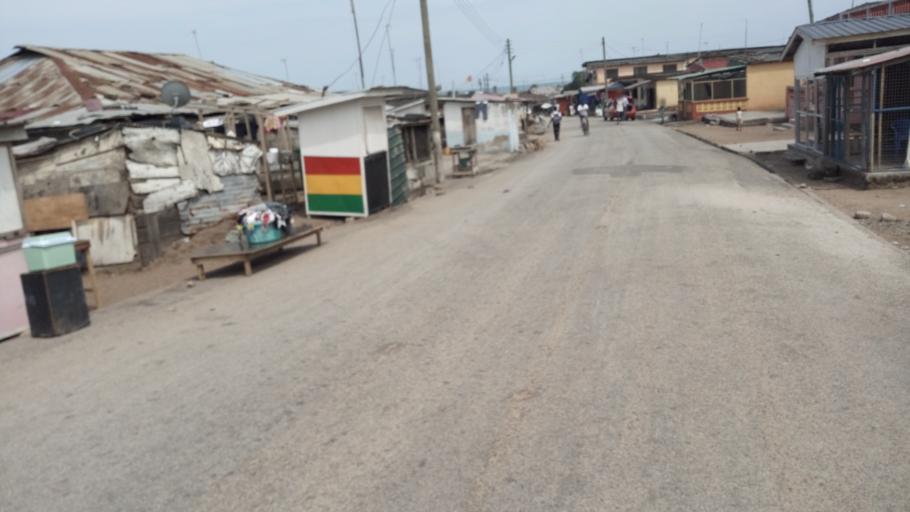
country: GH
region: Central
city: Winneba
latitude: 5.3460
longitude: -0.6215
